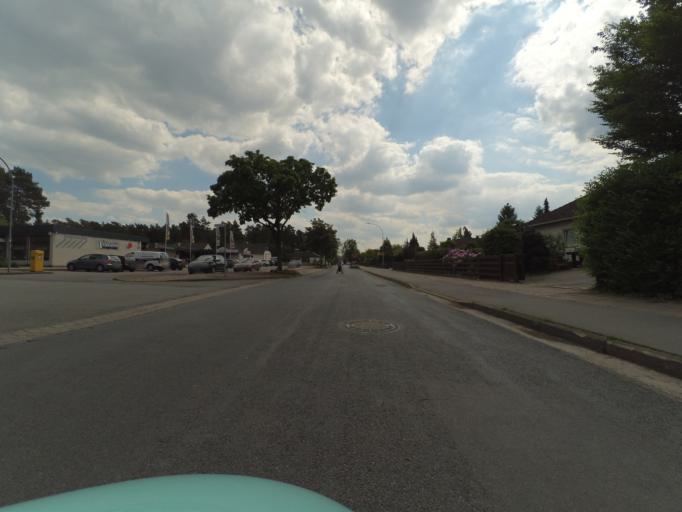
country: DE
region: Lower Saxony
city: Hambuhren
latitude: 52.6356
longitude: 9.9406
